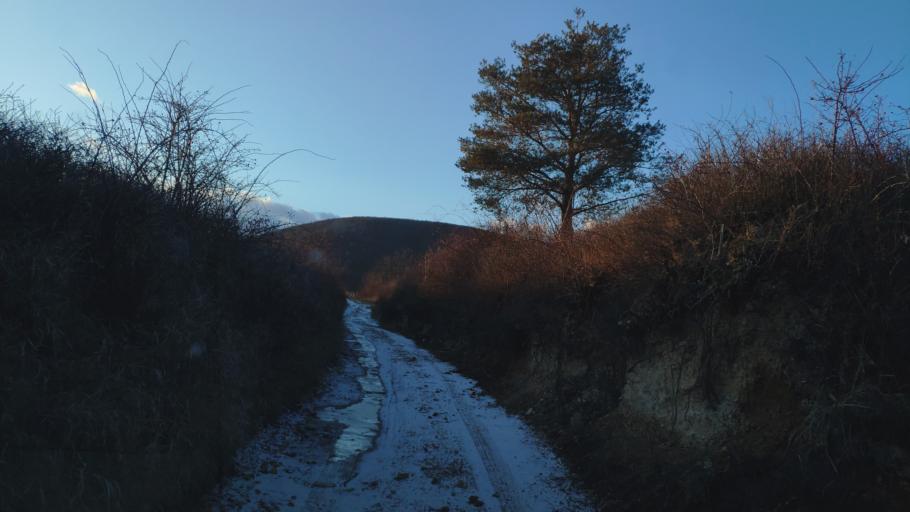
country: HU
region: Borsod-Abauj-Zemplen
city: Olaszliszka
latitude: 48.2746
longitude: 21.4034
